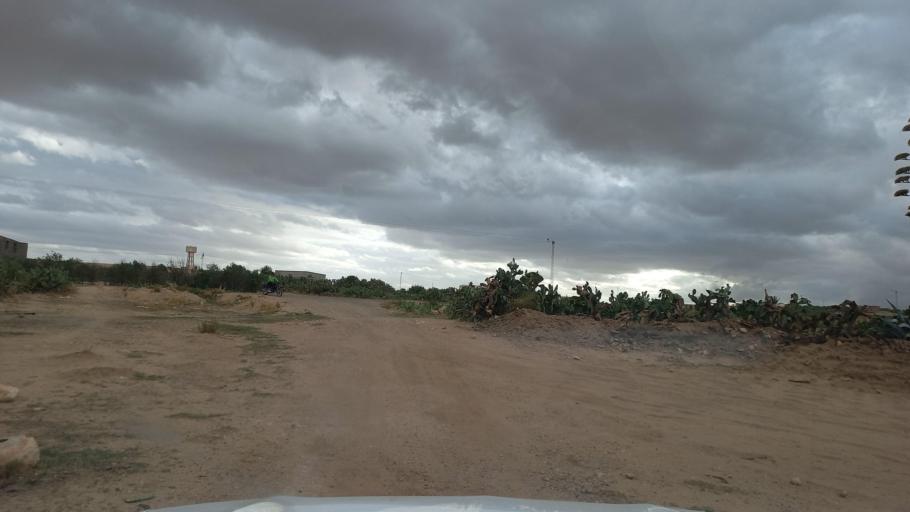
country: TN
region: Al Qasrayn
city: Kasserine
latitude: 35.2779
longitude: 8.9502
